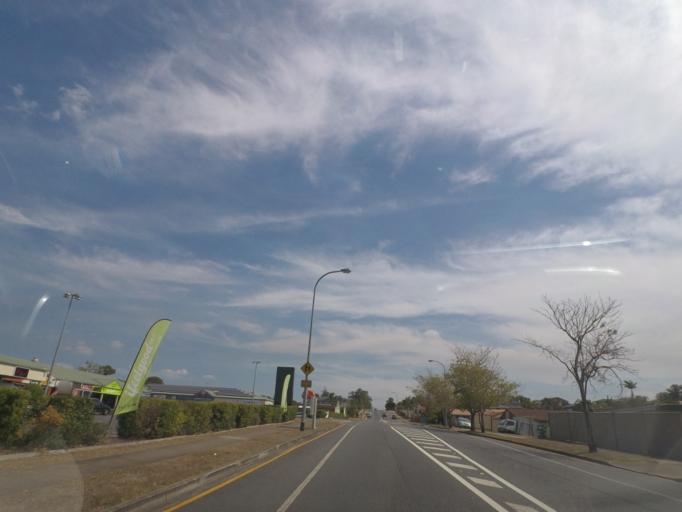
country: AU
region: Queensland
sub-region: Brisbane
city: Sunnybank Hills
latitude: -27.5965
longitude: 153.0648
